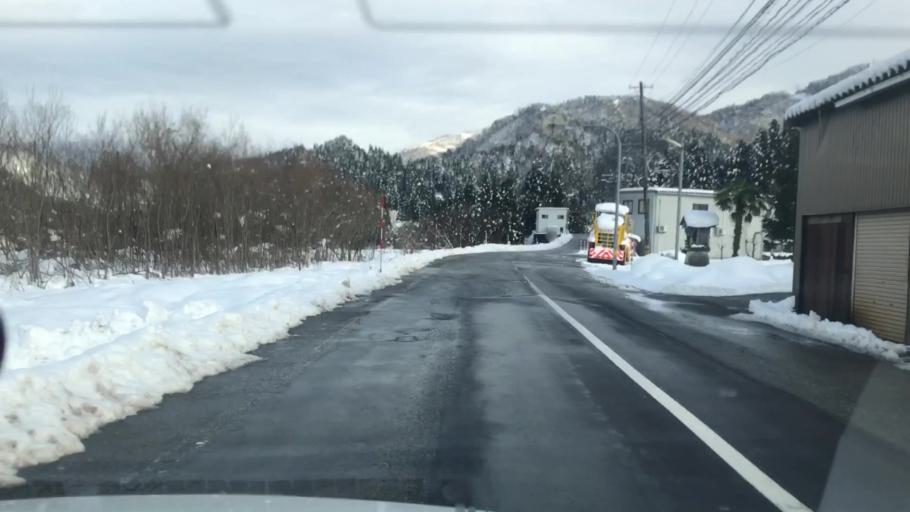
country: JP
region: Toyama
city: Kamiichi
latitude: 36.5700
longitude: 137.3586
